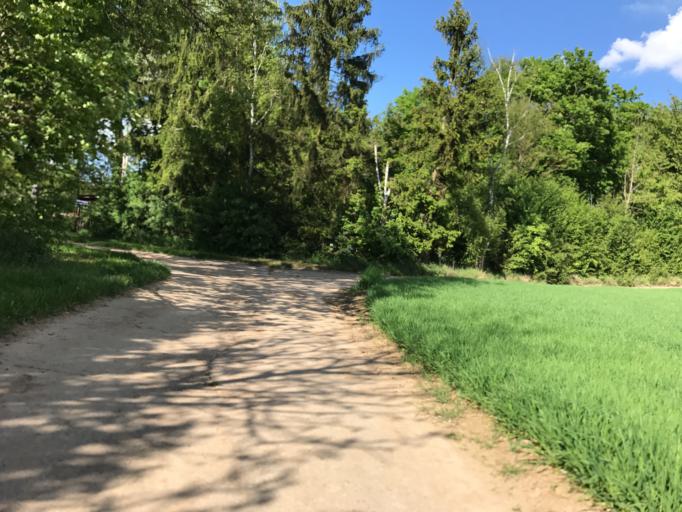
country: DE
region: Rheinland-Pfalz
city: Stadecken-Elsheim
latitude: 49.9391
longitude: 8.1214
